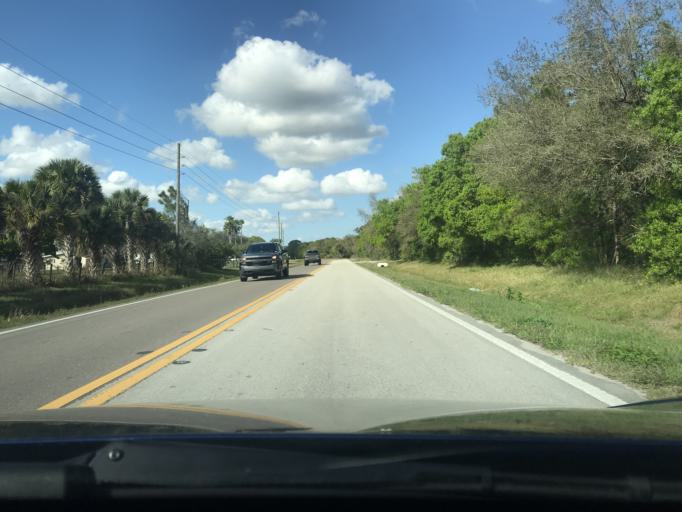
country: US
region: Florida
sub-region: Okeechobee County
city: Taylor Creek
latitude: 27.1954
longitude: -80.6944
